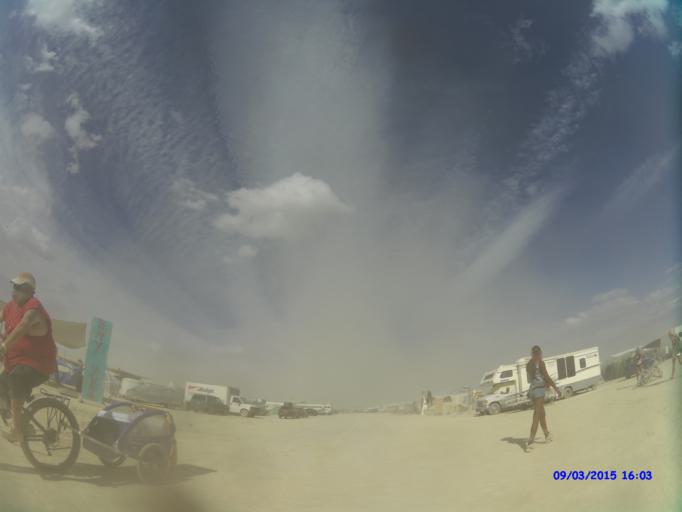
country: US
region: Nevada
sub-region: Pershing County
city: Lovelock
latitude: 40.7783
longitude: -119.2005
